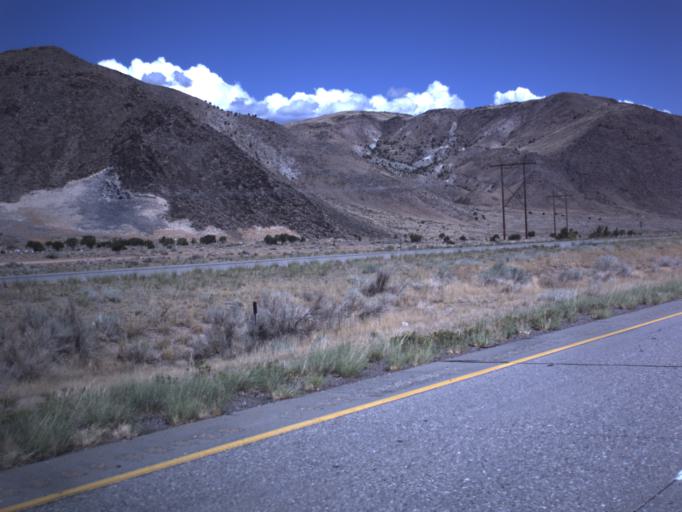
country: US
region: Utah
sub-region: Sevier County
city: Richfield
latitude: 38.7117
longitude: -112.1365
